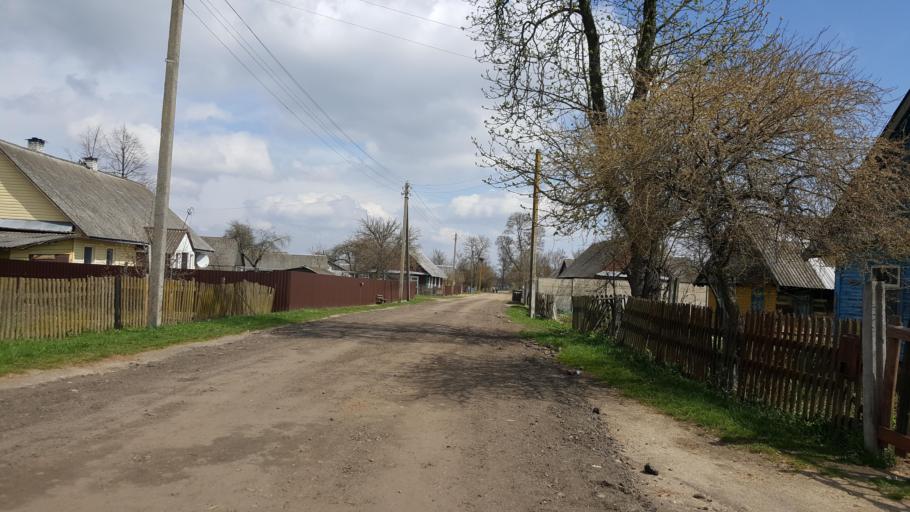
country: BY
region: Brest
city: Kamyanyets
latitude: 52.3582
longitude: 23.8989
